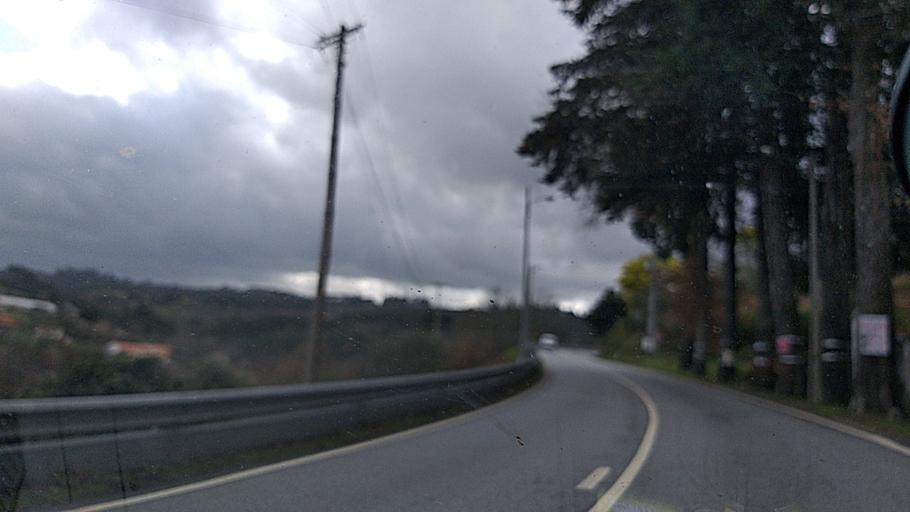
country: PT
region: Viseu
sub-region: Mangualde
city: Mangualde
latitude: 40.6361
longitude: -7.7403
